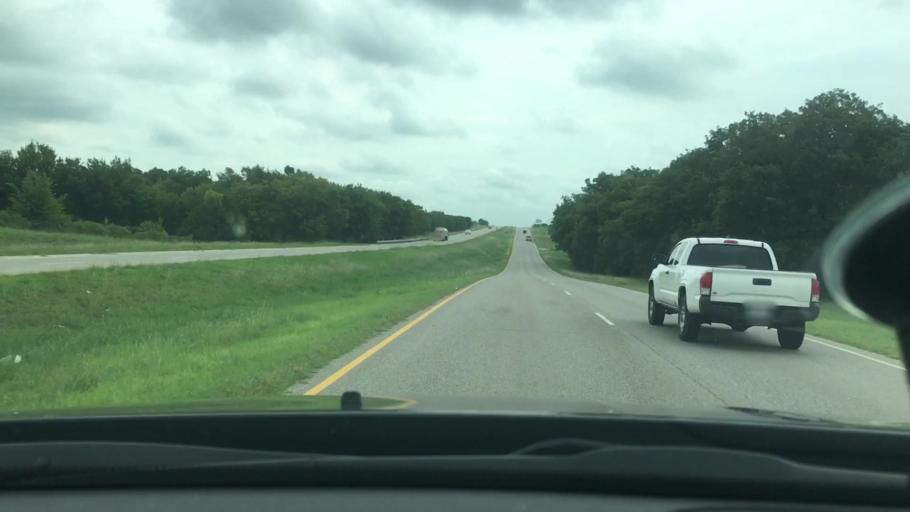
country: US
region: Oklahoma
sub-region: Carter County
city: Wilson
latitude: 34.1729
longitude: -97.4542
